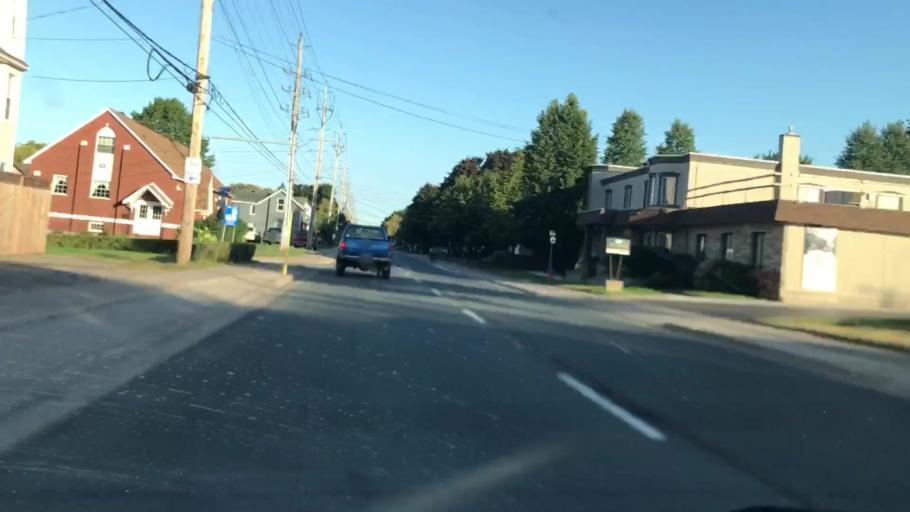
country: CA
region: Ontario
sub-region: Algoma
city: Sault Ste. Marie
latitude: 46.5117
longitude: -84.3282
